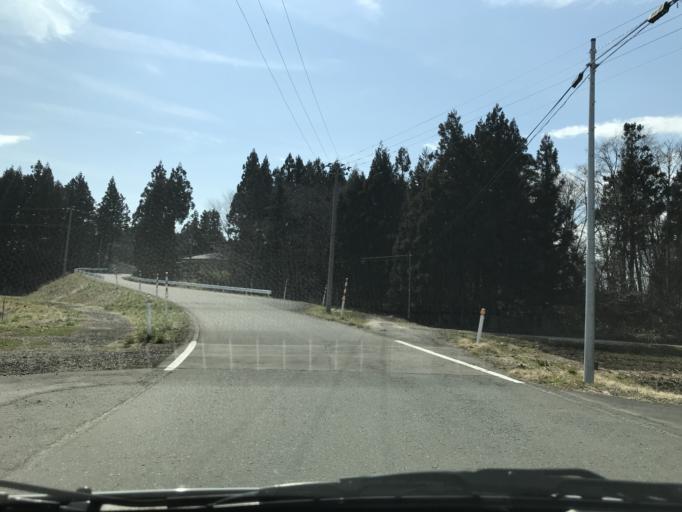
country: JP
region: Iwate
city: Mizusawa
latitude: 39.1190
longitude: 141.0437
